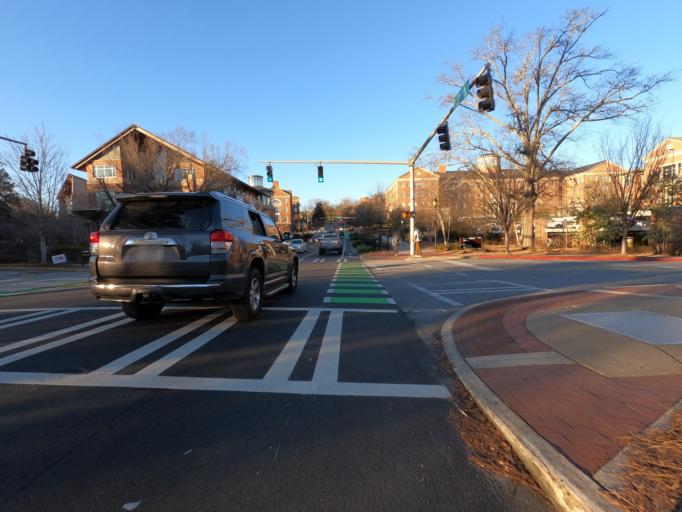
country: US
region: Georgia
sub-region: Clarke County
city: Athens
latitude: 33.9502
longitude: -83.3772
